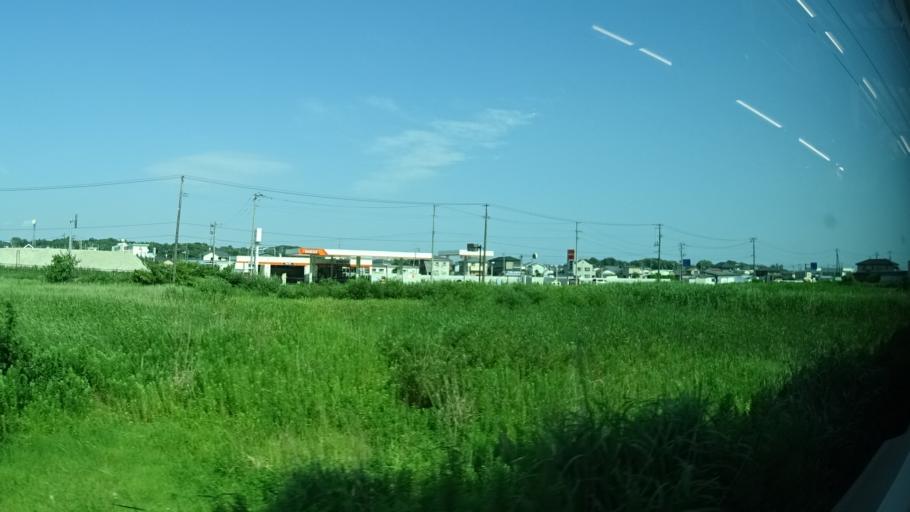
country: JP
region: Miyagi
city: Matsushima
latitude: 38.3888
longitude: 141.0666
